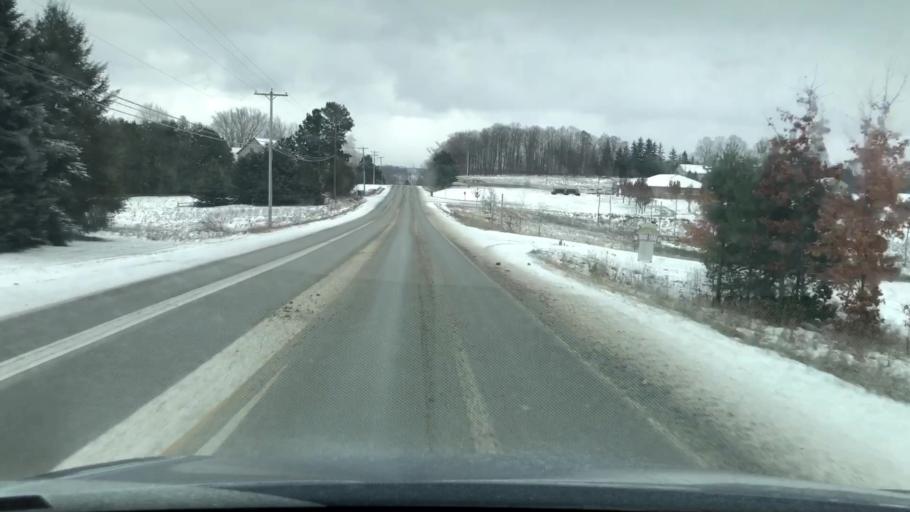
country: US
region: Michigan
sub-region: Grand Traverse County
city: Traverse City
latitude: 44.7155
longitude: -85.6353
